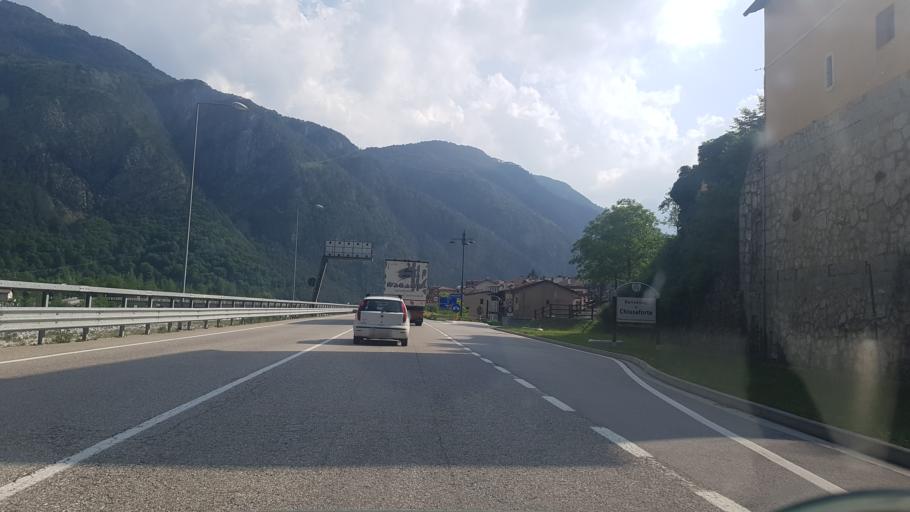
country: IT
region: Friuli Venezia Giulia
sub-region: Provincia di Udine
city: Chiusaforte
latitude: 46.4113
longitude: 13.3135
